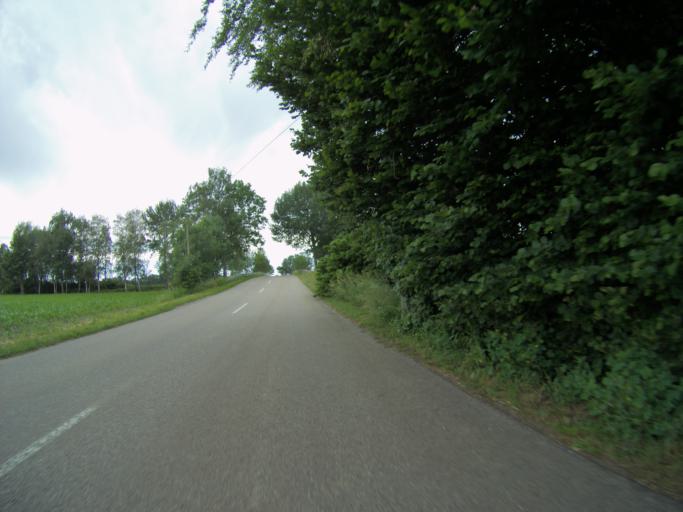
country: DE
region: Bavaria
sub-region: Upper Bavaria
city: Langenbach
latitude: 48.3868
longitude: 11.8453
